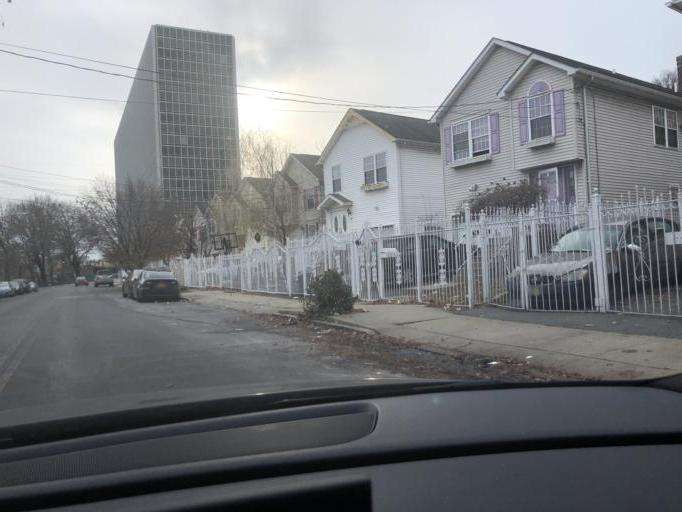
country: US
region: New Jersey
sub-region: Hudson County
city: East Newark
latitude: 40.7523
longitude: -74.1782
